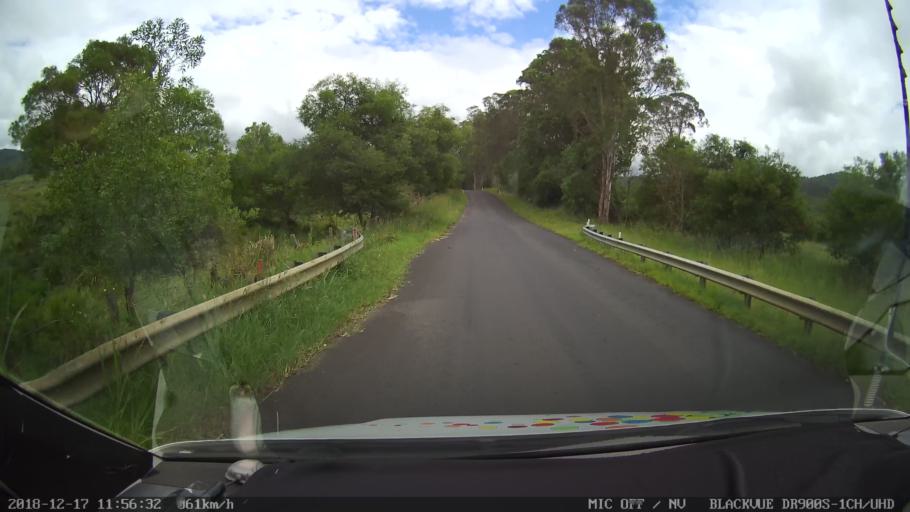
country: AU
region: New South Wales
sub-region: Kyogle
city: Kyogle
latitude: -28.5468
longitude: 152.5803
